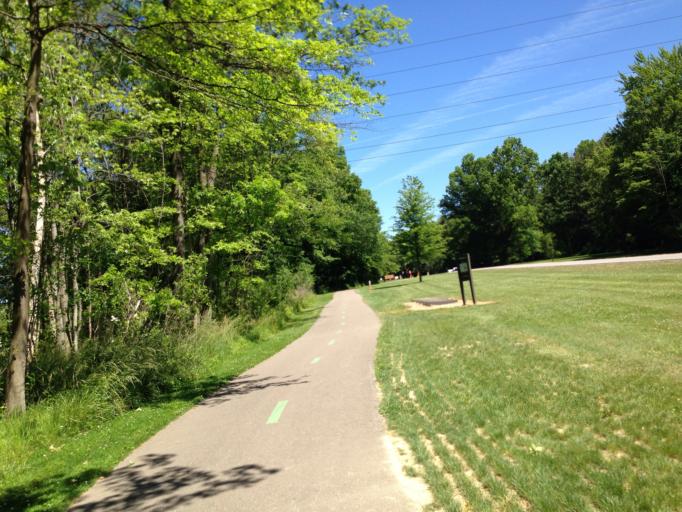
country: US
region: Ohio
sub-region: Cuyahoga County
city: Berea
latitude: 41.3528
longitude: -81.8513
